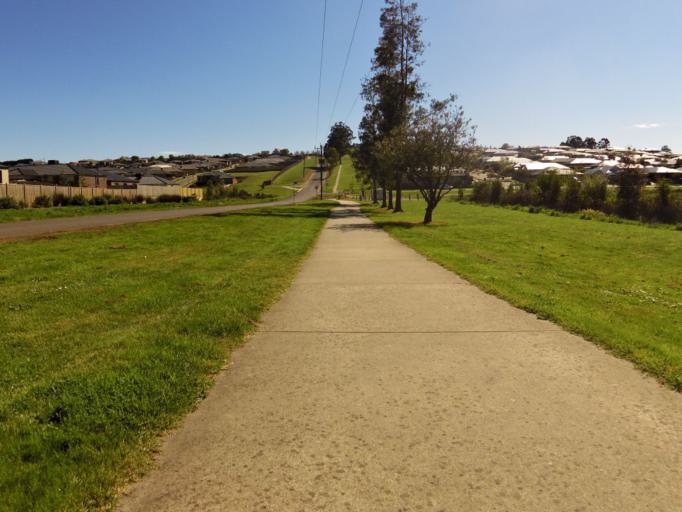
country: AU
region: Victoria
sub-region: Baw Baw
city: Warragul
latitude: -38.1314
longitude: 145.8638
